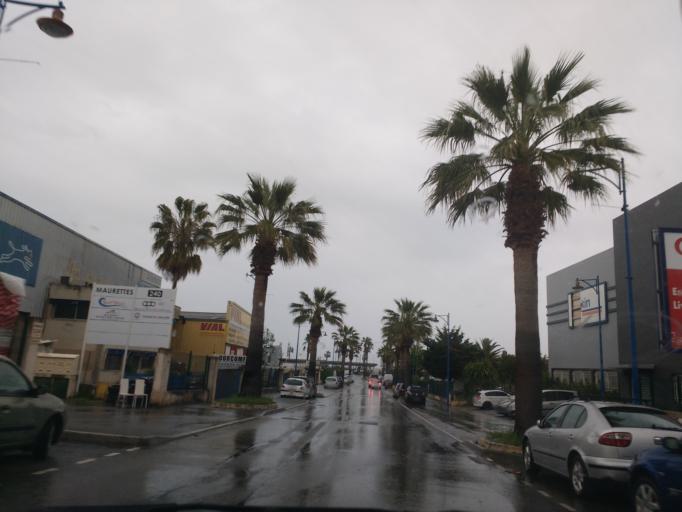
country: FR
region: Provence-Alpes-Cote d'Azur
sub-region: Departement des Alpes-Maritimes
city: Biot
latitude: 43.6304
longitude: 7.1310
